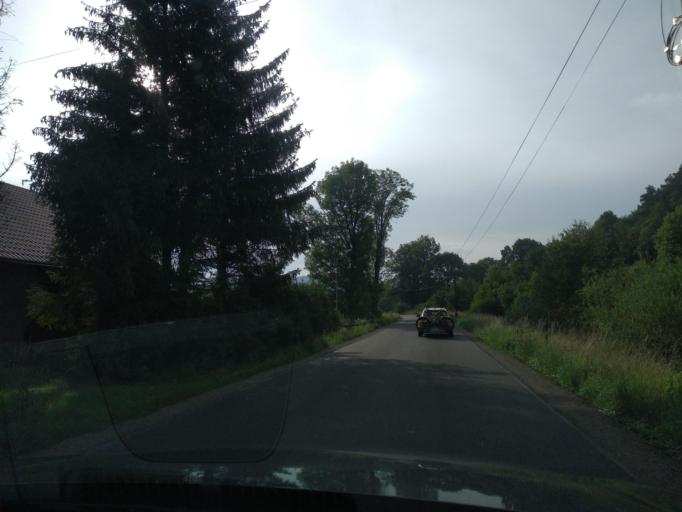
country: PL
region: Subcarpathian Voivodeship
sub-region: Powiat sanocki
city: Sanok
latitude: 49.6132
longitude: 22.2792
